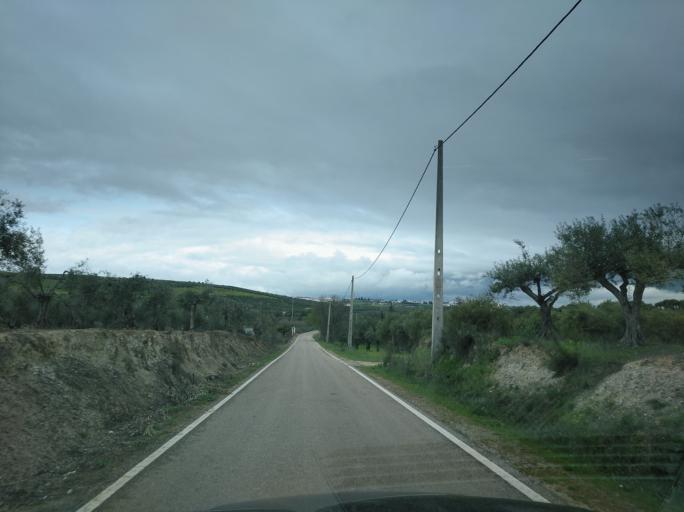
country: PT
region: Portalegre
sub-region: Campo Maior
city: Campo Maior
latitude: 38.9929
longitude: -7.0486
